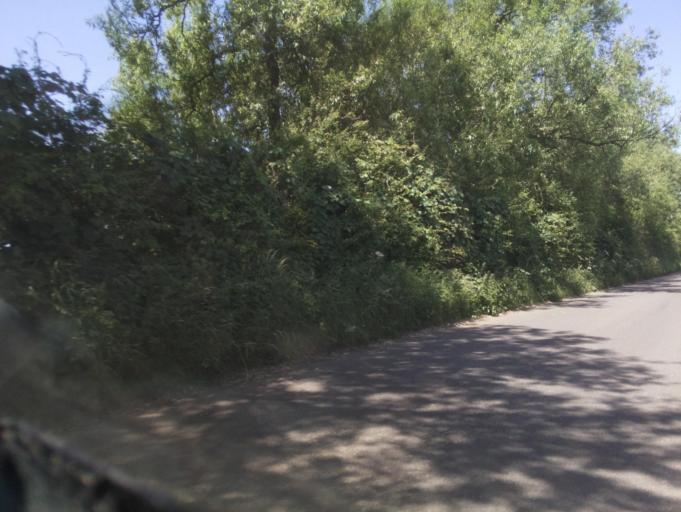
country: GB
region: England
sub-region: Wiltshire
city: Bremhill
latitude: 51.5005
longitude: -2.0495
